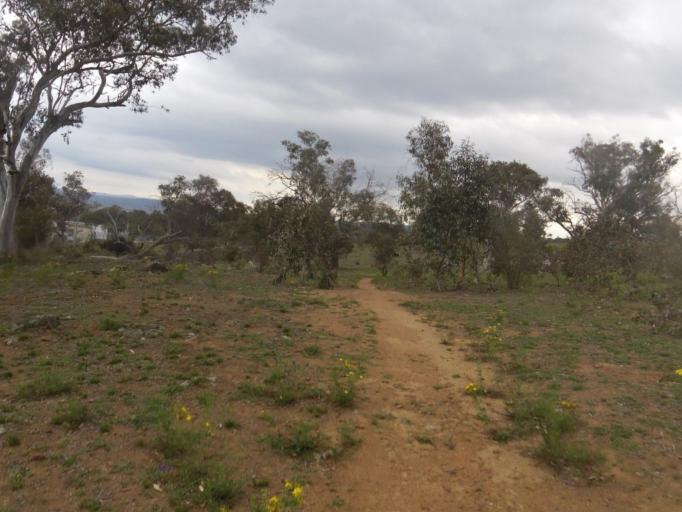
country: AU
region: Australian Capital Territory
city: Forrest
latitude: -35.3463
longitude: 149.1350
